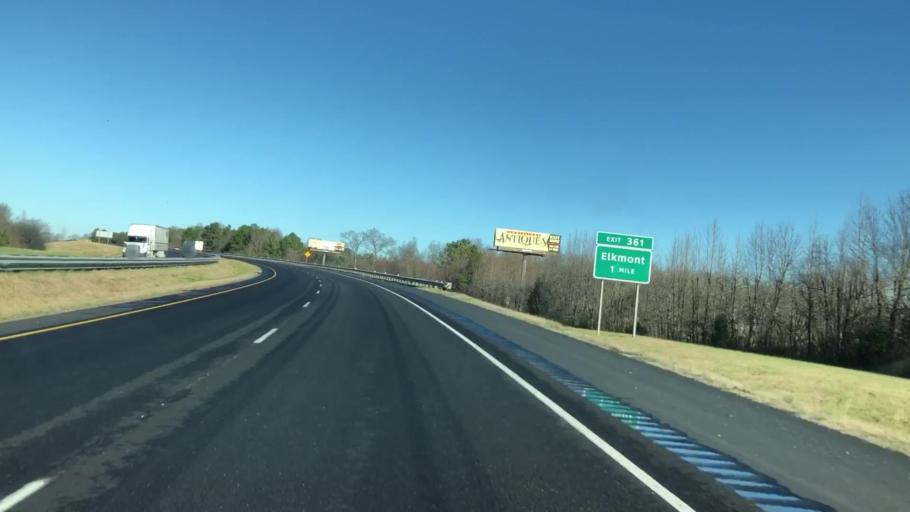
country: US
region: Alabama
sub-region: Limestone County
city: Ardmore
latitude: 34.9029
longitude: -86.9053
